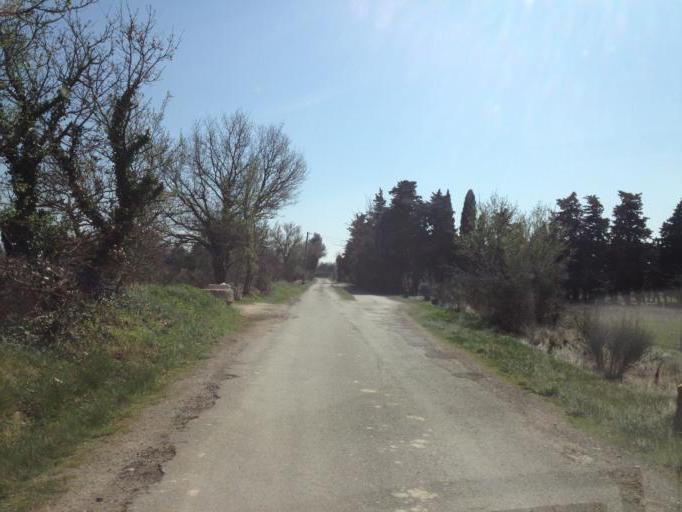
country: FR
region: Provence-Alpes-Cote d'Azur
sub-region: Departement du Vaucluse
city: Jonquieres
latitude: 44.0973
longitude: 4.9174
